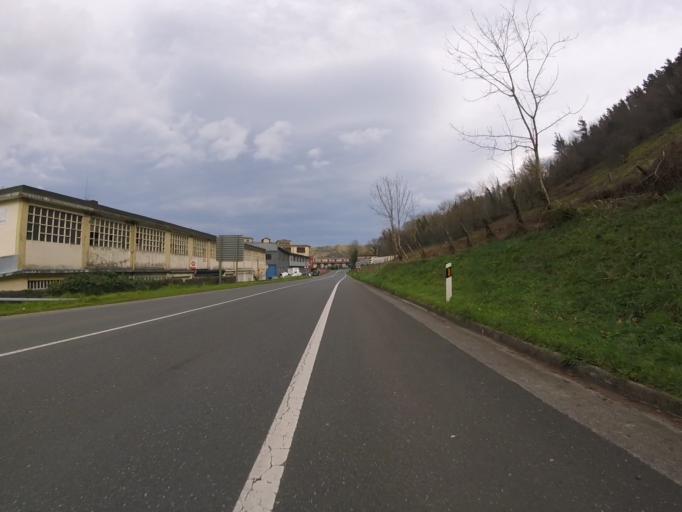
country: ES
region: Basque Country
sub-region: Provincia de Guipuzcoa
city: Cestona
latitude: 43.2525
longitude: -2.2604
